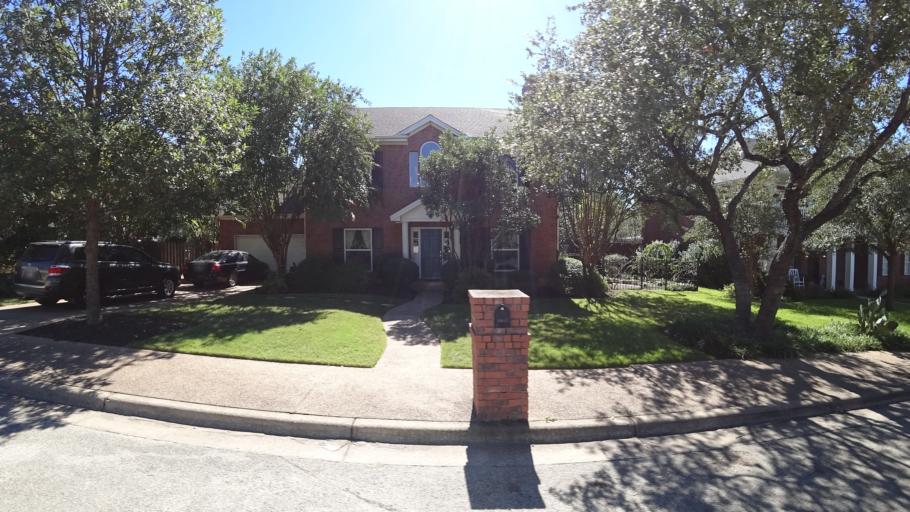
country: US
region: Texas
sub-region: Travis County
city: West Lake Hills
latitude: 30.3396
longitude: -97.7800
